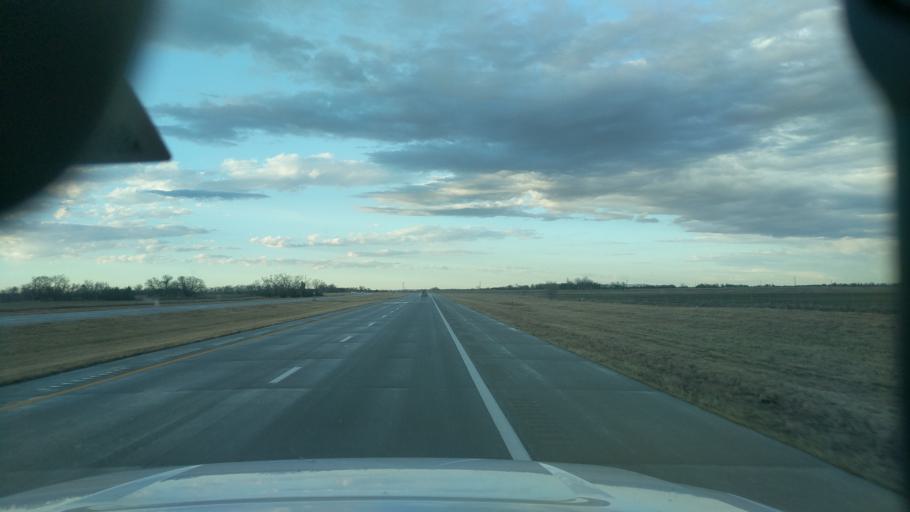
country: US
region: Kansas
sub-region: Harvey County
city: Hesston
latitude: 38.1648
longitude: -97.4370
